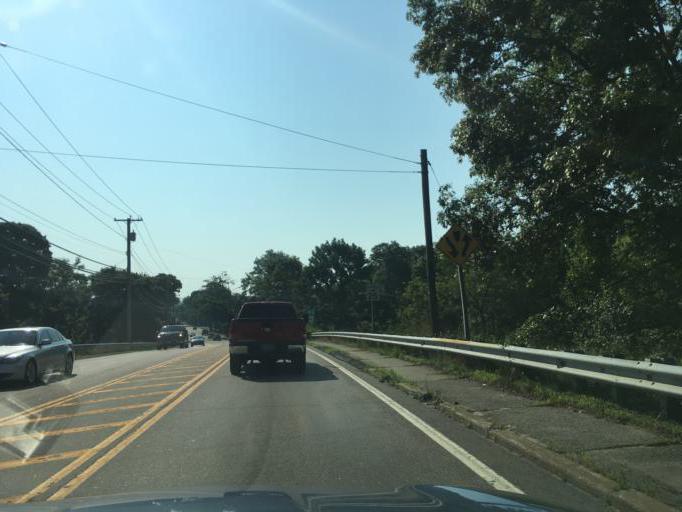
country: US
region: Rhode Island
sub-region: Washington County
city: Kingston
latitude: 41.4846
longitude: -71.5597
